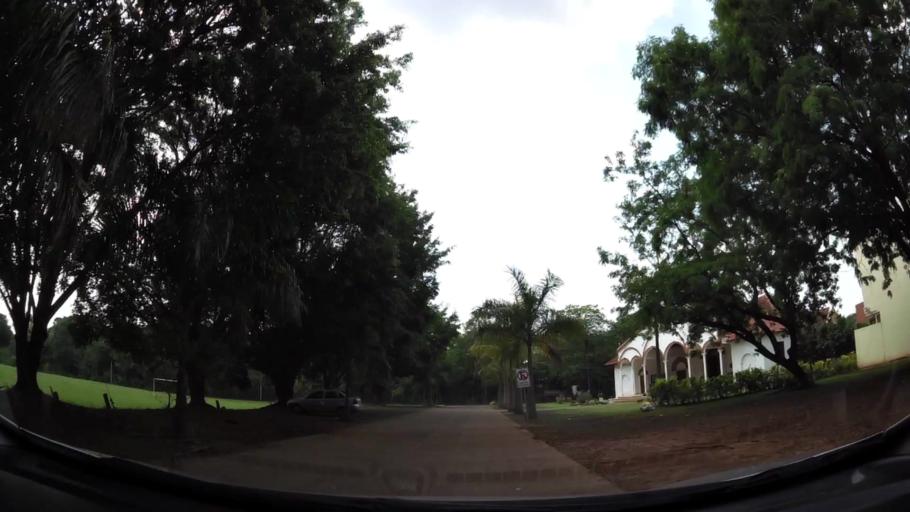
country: PY
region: Alto Parana
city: Ciudad del Este
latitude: -25.4755
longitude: -54.6217
